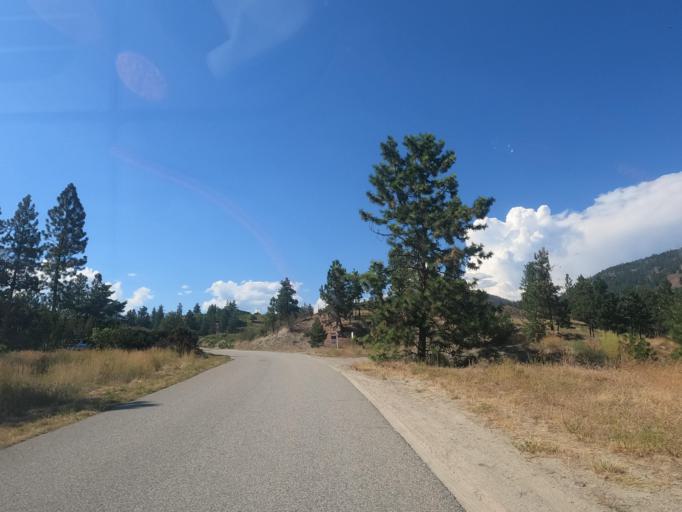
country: CA
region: British Columbia
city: Peachland
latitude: 49.7888
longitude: -119.7108
